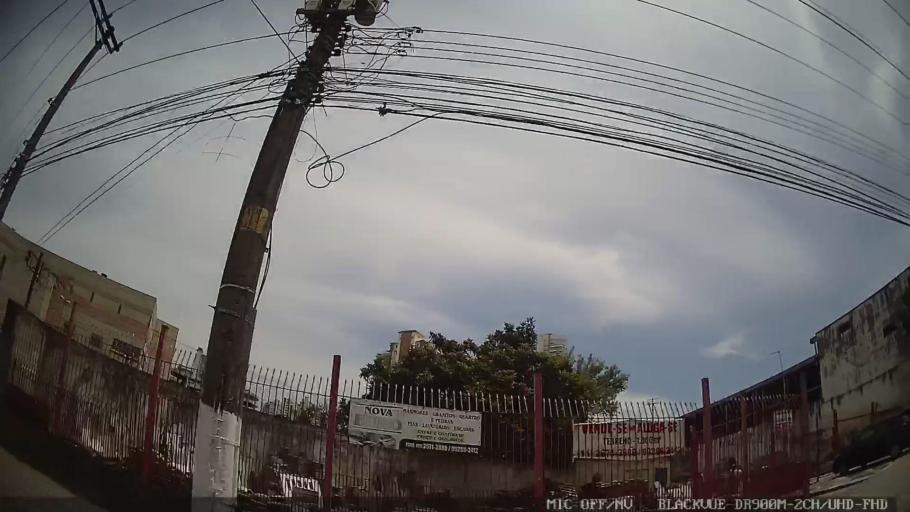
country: BR
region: Sao Paulo
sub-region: Sao Caetano Do Sul
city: Sao Caetano do Sul
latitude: -23.5625
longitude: -46.5579
